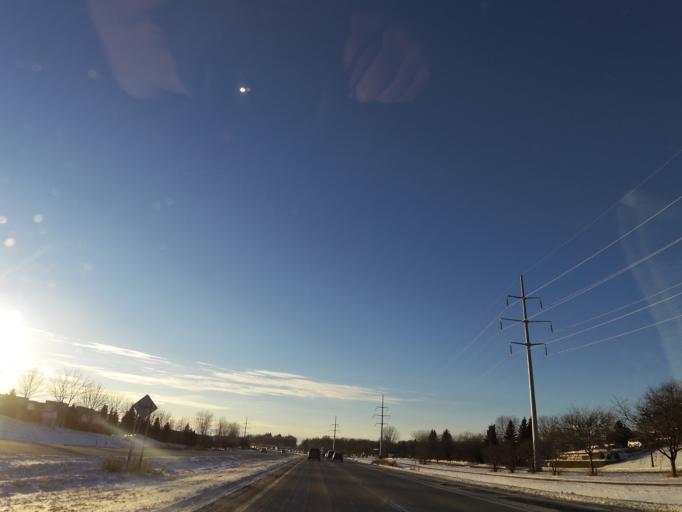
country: US
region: Minnesota
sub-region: Carver County
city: Chanhassen
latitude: 44.8620
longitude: -93.5165
